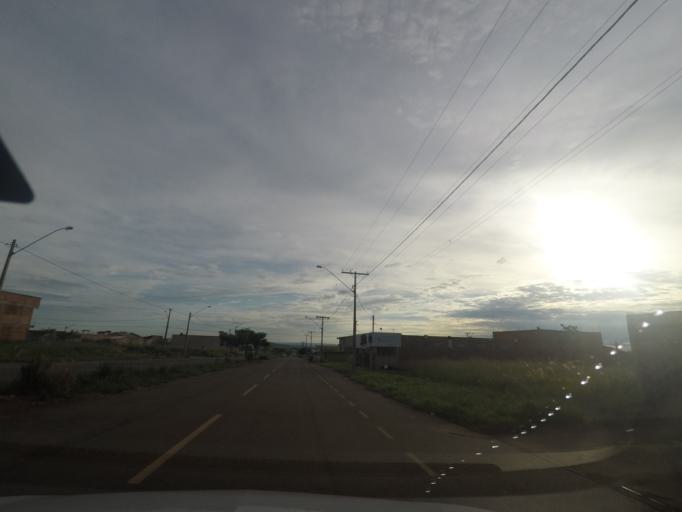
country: BR
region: Goias
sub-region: Trindade
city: Trindade
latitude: -16.7290
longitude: -49.4096
